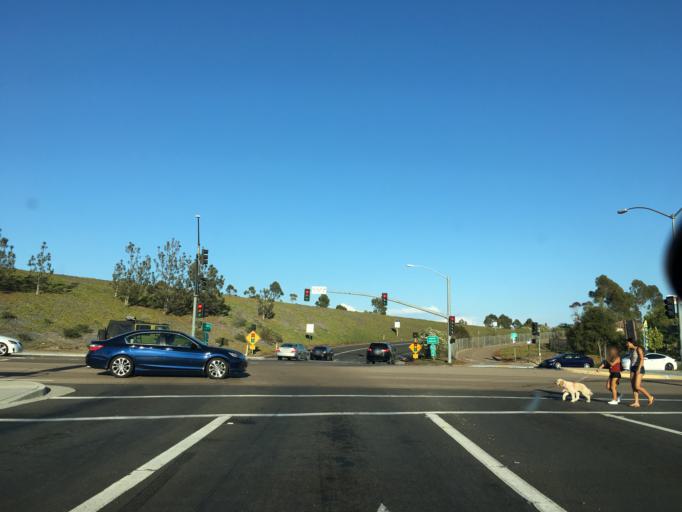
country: US
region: California
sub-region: San Diego County
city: Fairbanks Ranch
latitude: 32.9581
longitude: -117.1533
